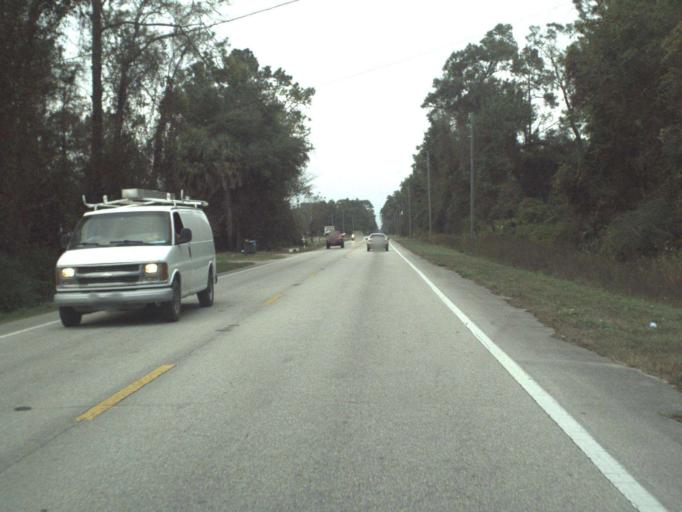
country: US
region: Florida
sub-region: Leon County
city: Woodville
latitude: 30.2420
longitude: -84.2321
